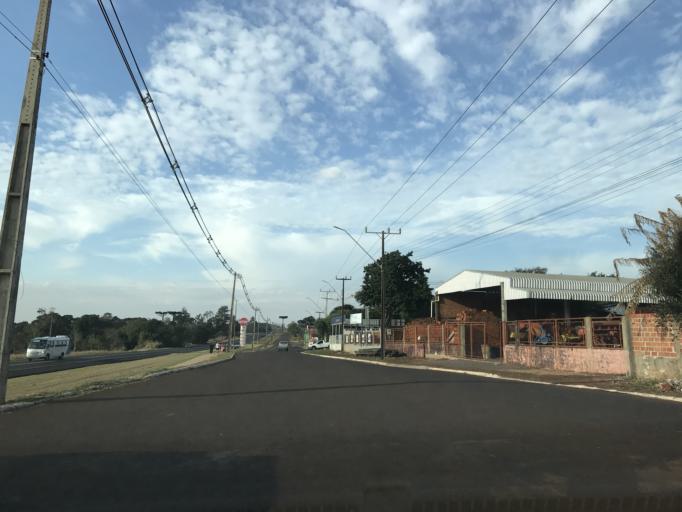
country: BR
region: Parana
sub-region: Cascavel
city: Cascavel
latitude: -25.0468
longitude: -53.6108
